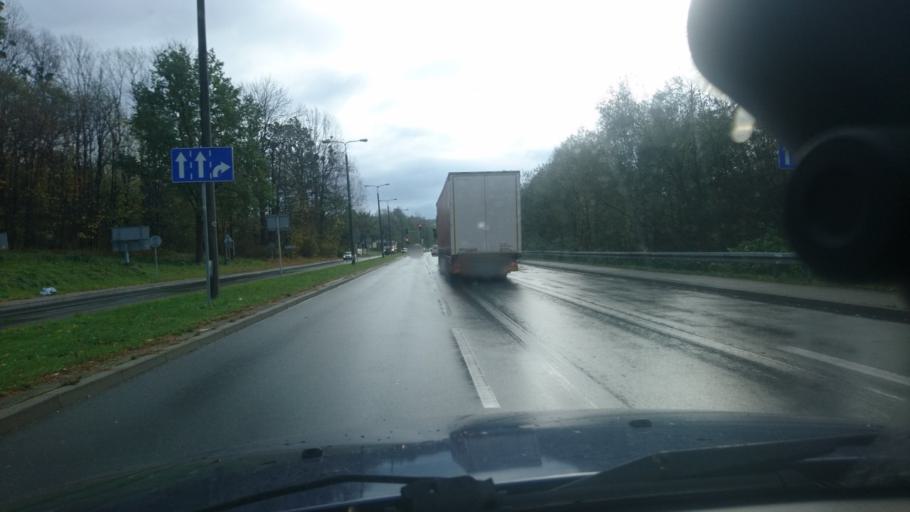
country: PL
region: Silesian Voivodeship
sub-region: Powiat bielski
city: Mazancowice
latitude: 49.8402
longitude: 19.0030
